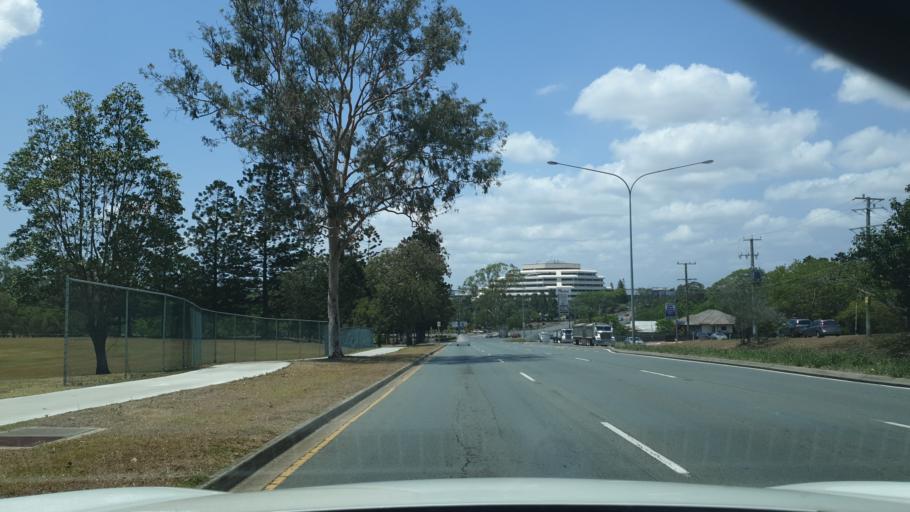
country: AU
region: Queensland
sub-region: Brisbane
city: Chermside West
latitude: -27.3769
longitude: 153.0279
